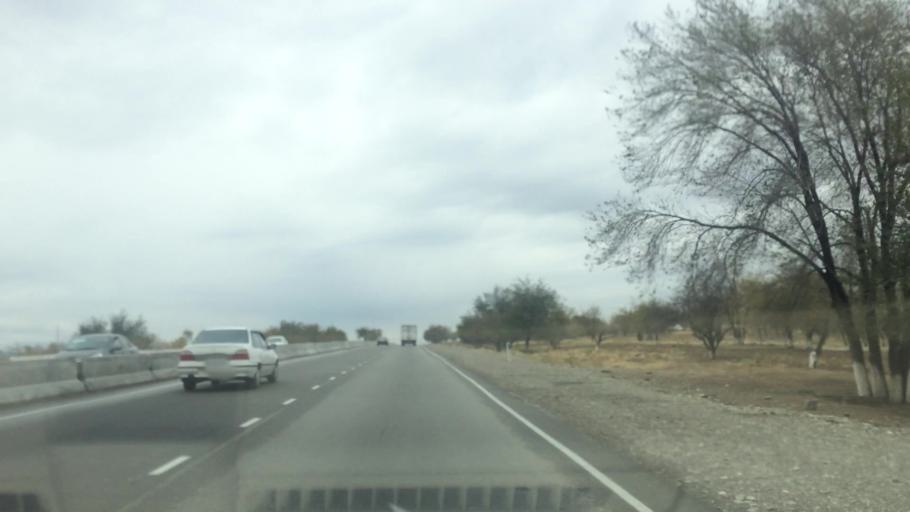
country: UZ
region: Samarqand
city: Bulung'ur
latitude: 39.9300
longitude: 67.5215
